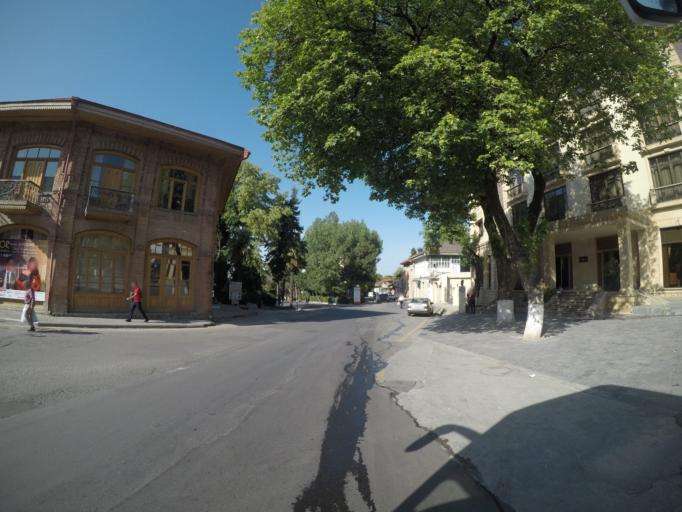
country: AZ
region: Shaki City
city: Sheki
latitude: 41.2032
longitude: 47.1784
